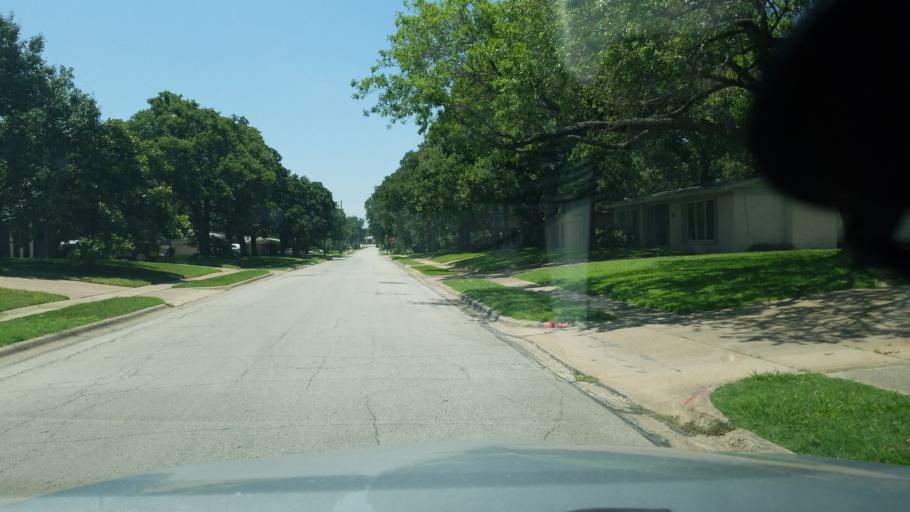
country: US
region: Texas
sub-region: Dallas County
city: Irving
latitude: 32.8350
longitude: -96.9683
